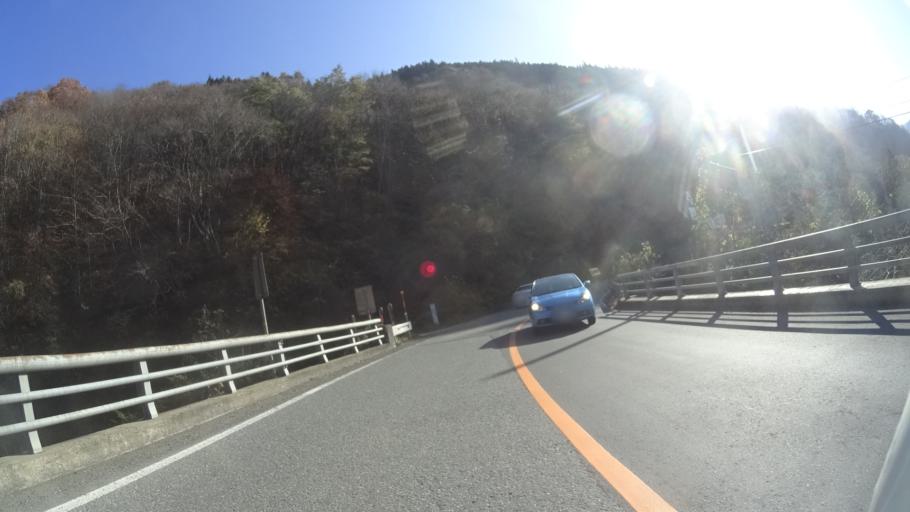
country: JP
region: Fukui
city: Ono
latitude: 35.8948
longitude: 136.6966
